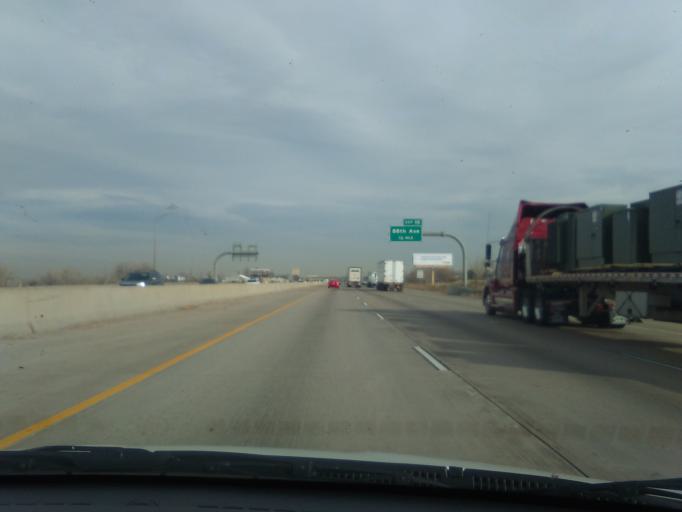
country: US
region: Colorado
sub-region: Adams County
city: Derby
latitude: 39.8500
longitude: -104.9204
